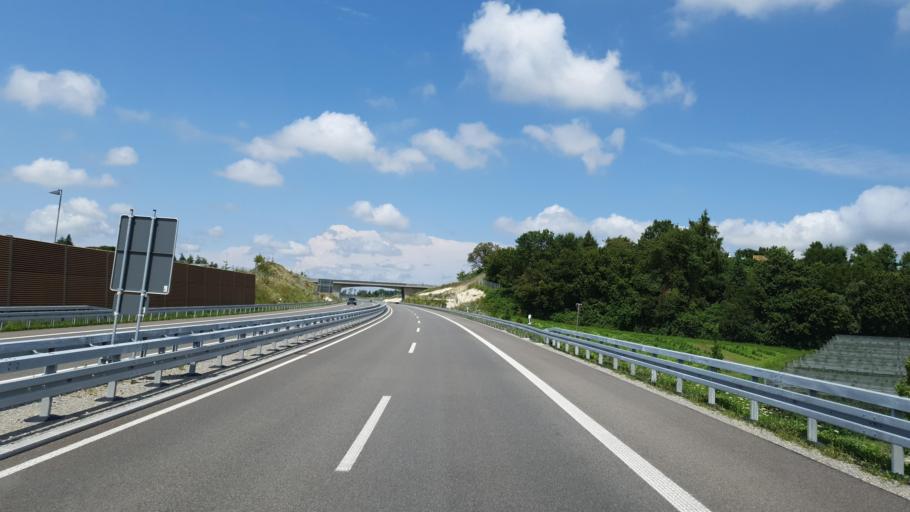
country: DE
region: Baden-Wuerttemberg
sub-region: Tuebingen Region
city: Friedrichshafen
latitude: 47.6783
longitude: 9.4459
